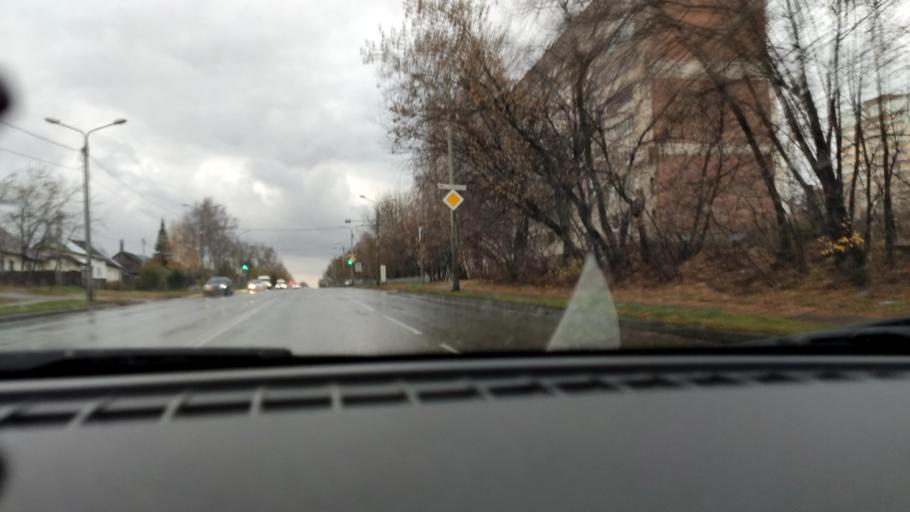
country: RU
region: Perm
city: Perm
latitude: 58.0648
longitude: 56.3643
